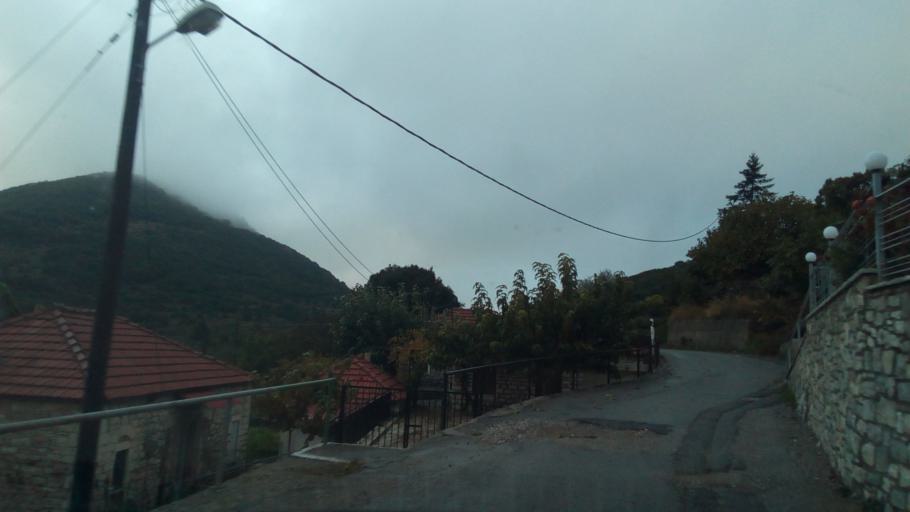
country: GR
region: West Greece
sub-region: Nomos Aitolias kai Akarnanias
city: Nafpaktos
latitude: 38.4846
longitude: 21.7697
